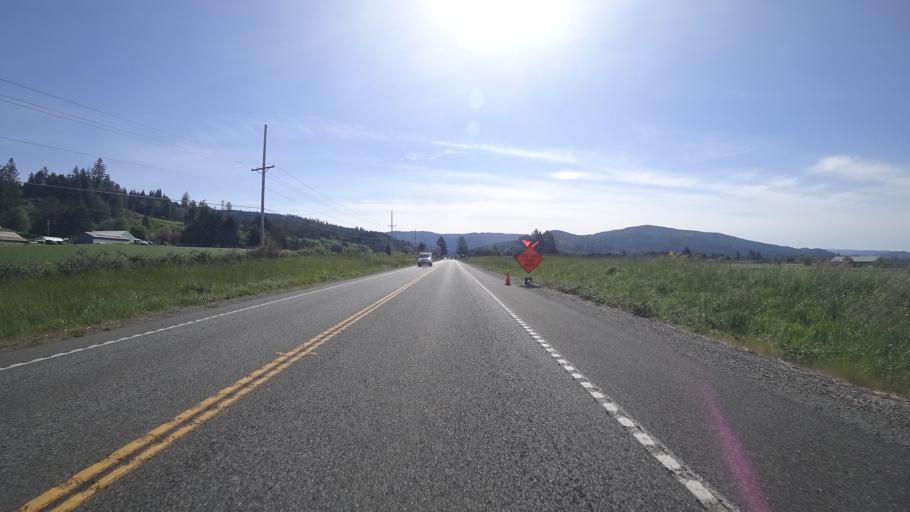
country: US
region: Oregon
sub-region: Curry County
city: Harbor
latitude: 41.9329
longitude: -124.1595
